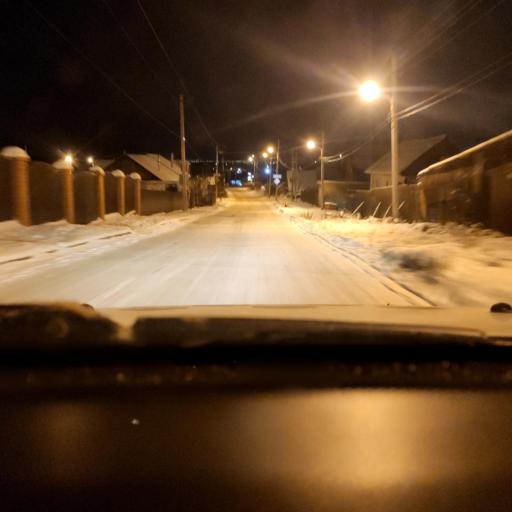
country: RU
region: Perm
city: Ferma
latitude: 57.9578
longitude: 56.3725
